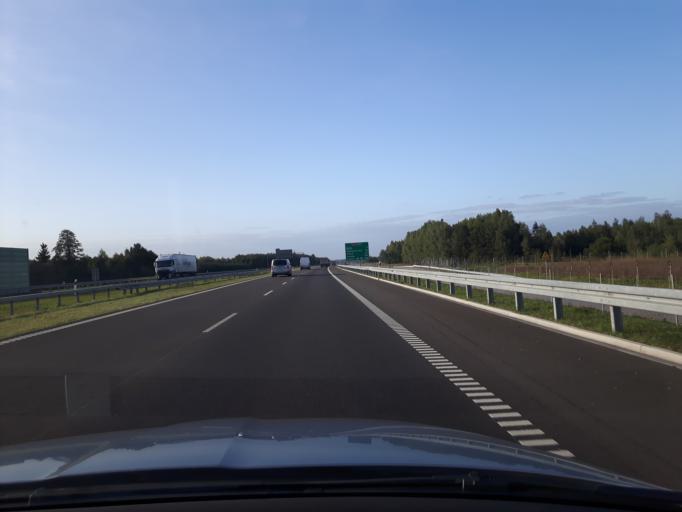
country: PL
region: Masovian Voivodeship
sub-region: Powiat radomski
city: Wolanow
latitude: 51.3821
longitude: 21.0201
